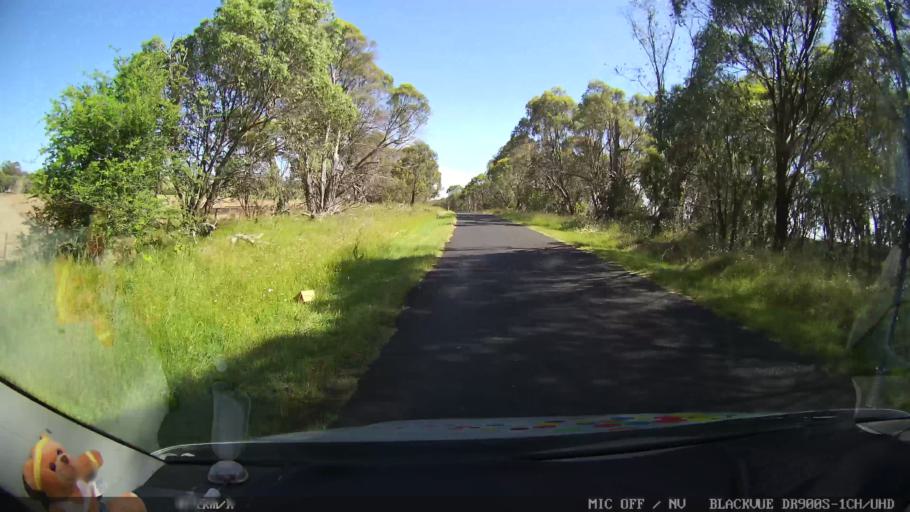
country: AU
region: New South Wales
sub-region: Guyra
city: Guyra
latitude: -30.0957
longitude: 151.6789
